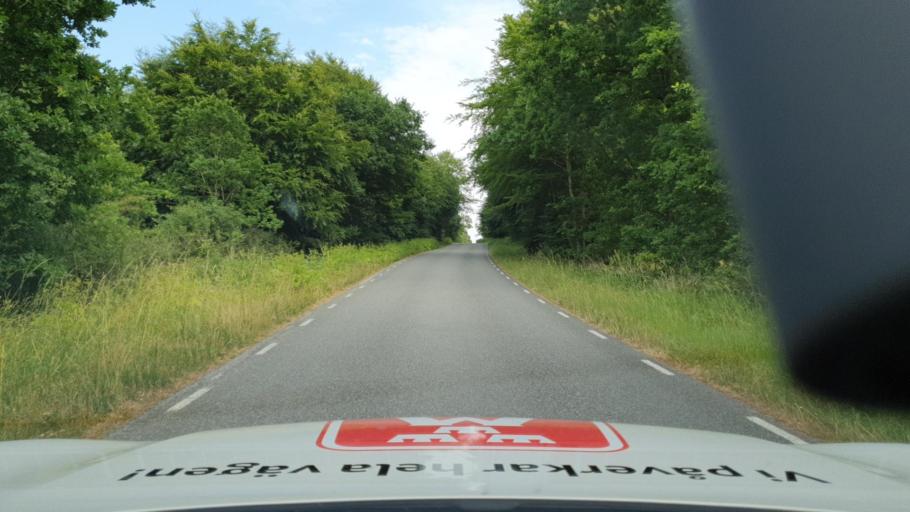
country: SE
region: Skane
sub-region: Kristianstads Kommun
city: Degeberga
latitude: 55.7000
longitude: 14.0536
